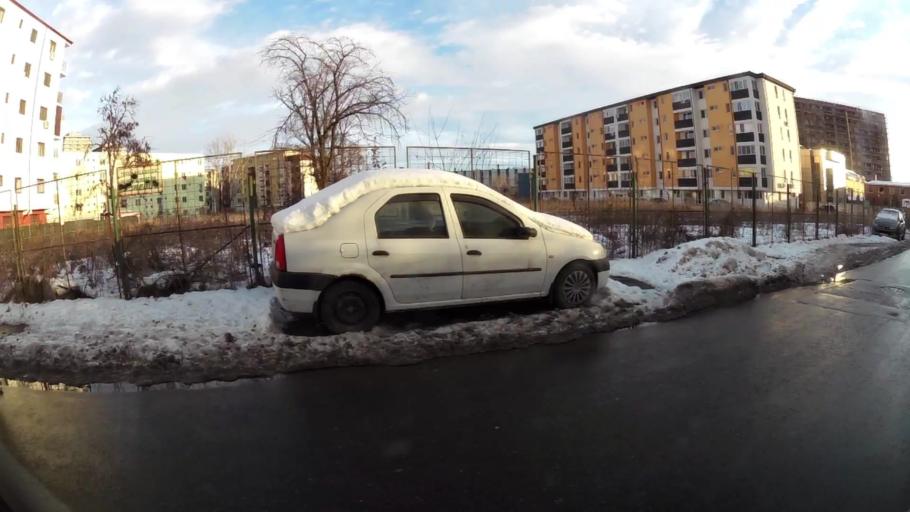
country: RO
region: Ilfov
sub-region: Comuna Popesti-Leordeni
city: Popesti-Leordeni
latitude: 44.3709
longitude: 26.1354
